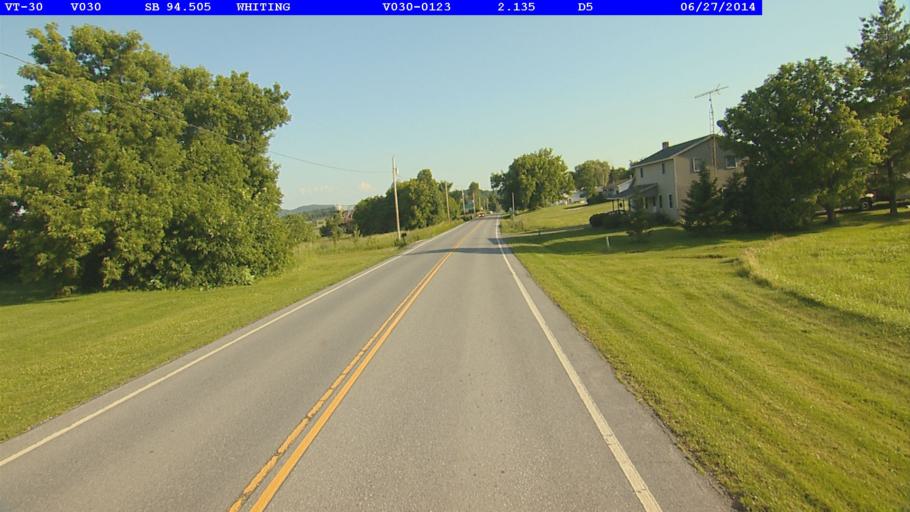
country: US
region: Vermont
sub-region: Rutland County
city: Brandon
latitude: 43.8682
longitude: -73.1996
